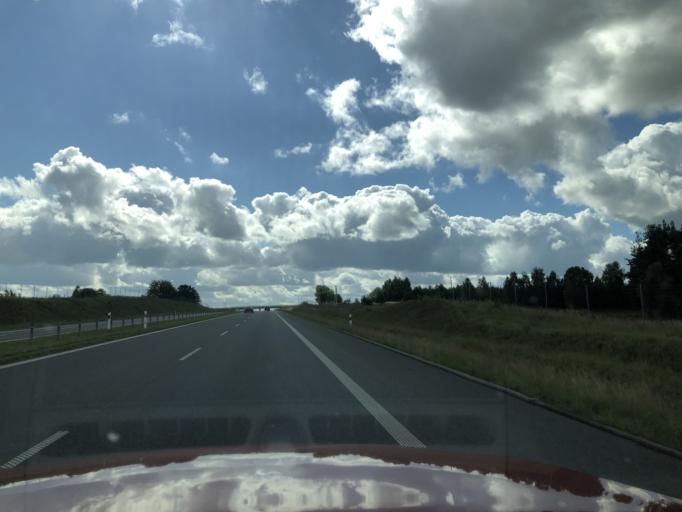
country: PL
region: West Pomeranian Voivodeship
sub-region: Powiat szczecinecki
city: Szczecinek
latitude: 53.6726
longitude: 16.7371
